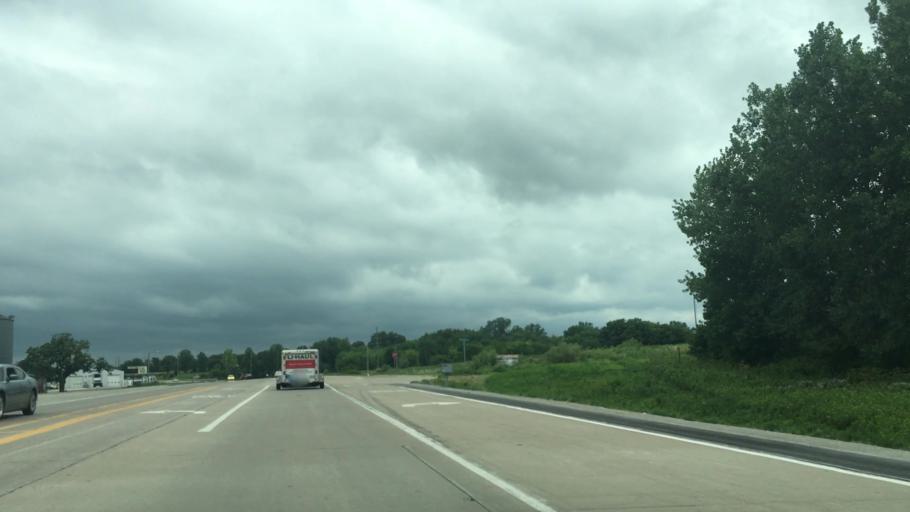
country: US
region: Iowa
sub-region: Johnson County
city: Tiffin
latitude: 41.6987
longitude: -91.6268
